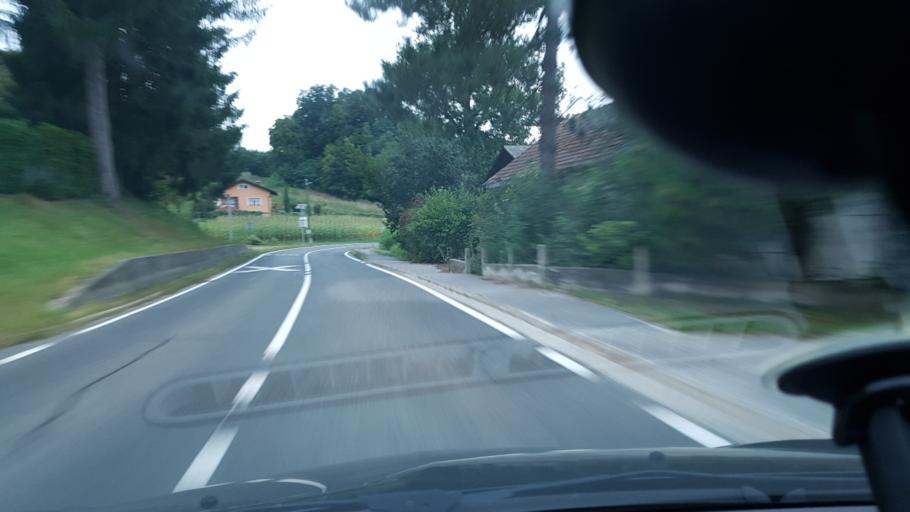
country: HR
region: Krapinsko-Zagorska
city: Pregrada
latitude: 46.2076
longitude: 15.7517
